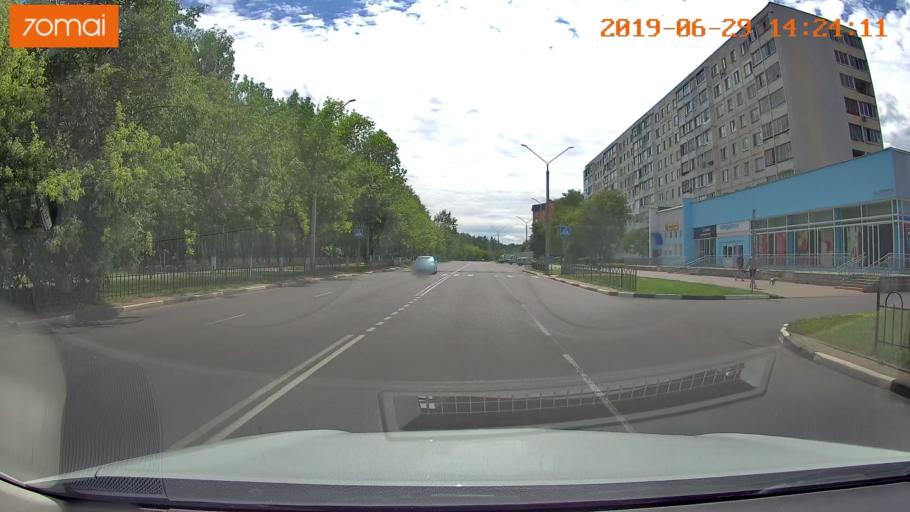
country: BY
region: Minsk
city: Salihorsk
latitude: 52.7817
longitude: 27.5504
